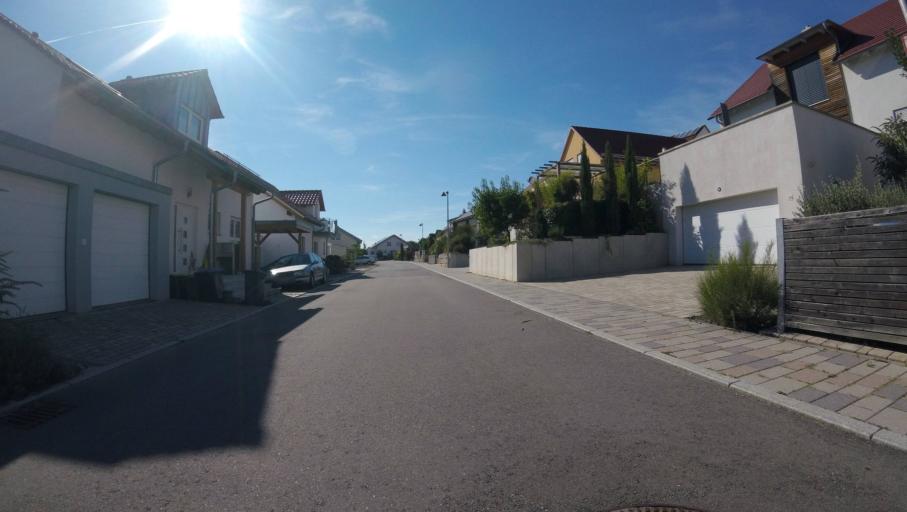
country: DE
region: Baden-Wuerttemberg
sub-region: Regierungsbezirk Stuttgart
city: Kirchberg an der Murr
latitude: 48.9441
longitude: 9.3363
